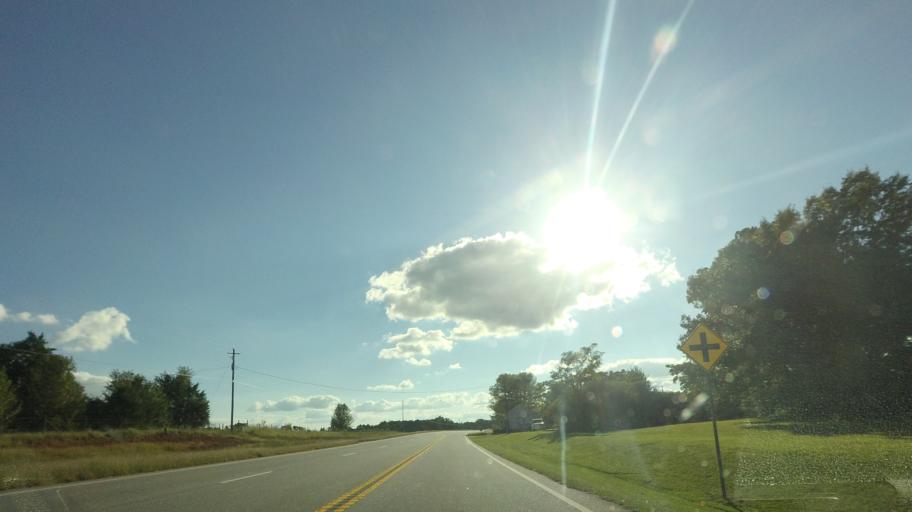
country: US
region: Georgia
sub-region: Upson County
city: Thomaston
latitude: 32.9338
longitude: -84.2601
